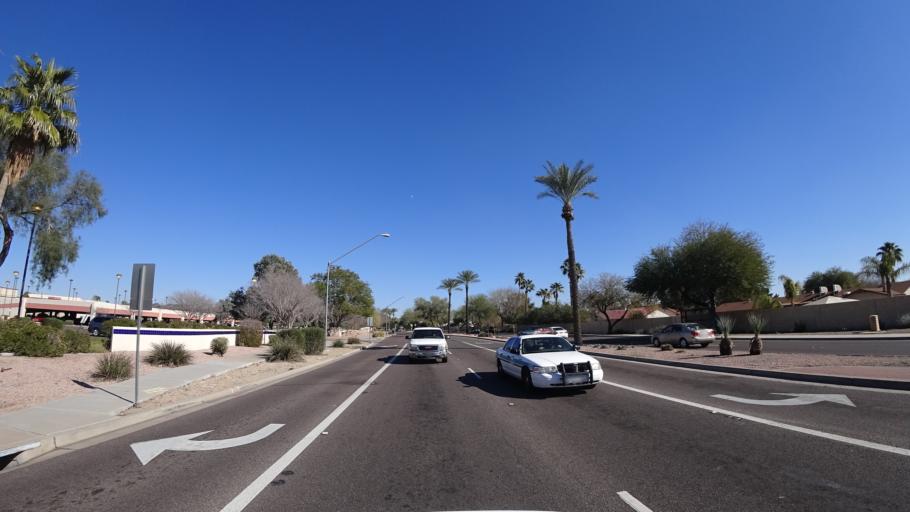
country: US
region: Arizona
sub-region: Maricopa County
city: Peoria
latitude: 33.6529
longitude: -112.2027
